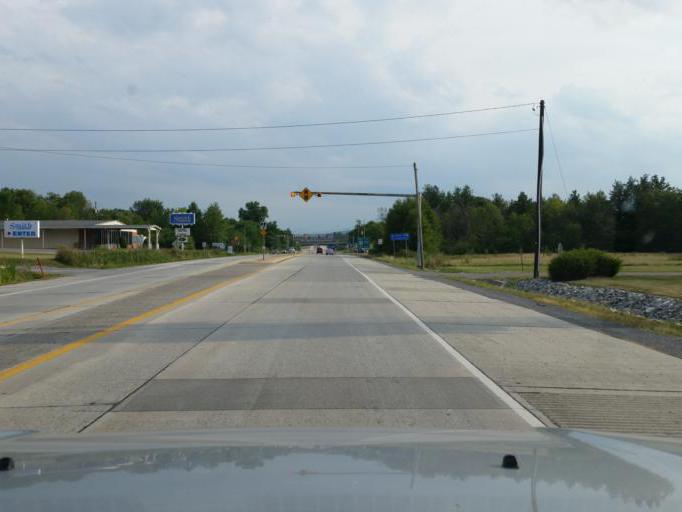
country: US
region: Pennsylvania
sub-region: Blair County
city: Duncansville
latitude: 40.4504
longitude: -78.4318
